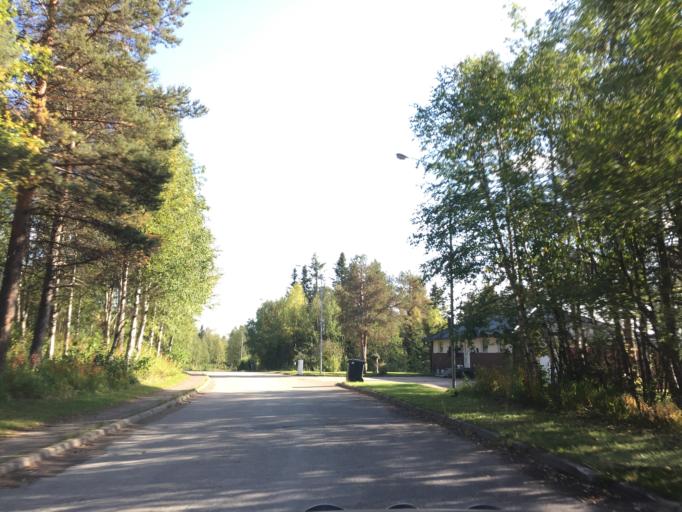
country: SE
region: Norrbotten
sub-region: Gallivare Kommun
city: Malmberget
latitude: 67.6503
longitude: 21.0455
